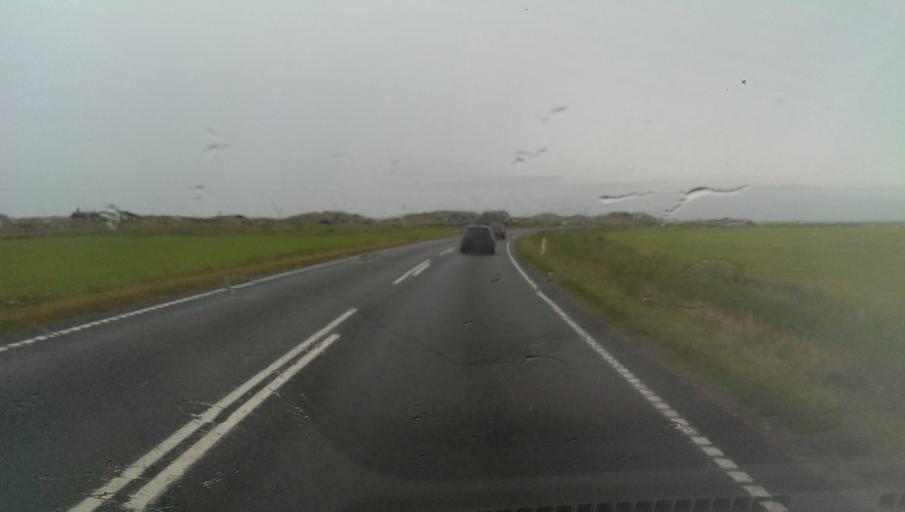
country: DK
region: Central Jutland
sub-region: Ringkobing-Skjern Kommune
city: Ringkobing
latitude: 56.1501
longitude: 8.1250
